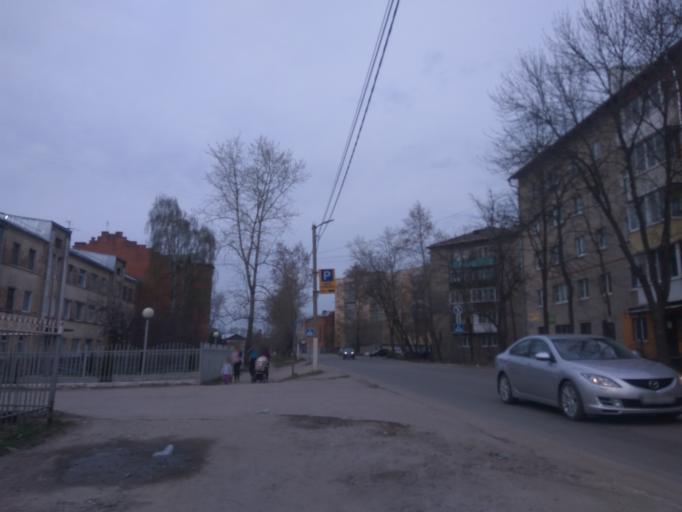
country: RU
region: Vladimir
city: Aleksandrov
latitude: 56.3996
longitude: 38.7087
